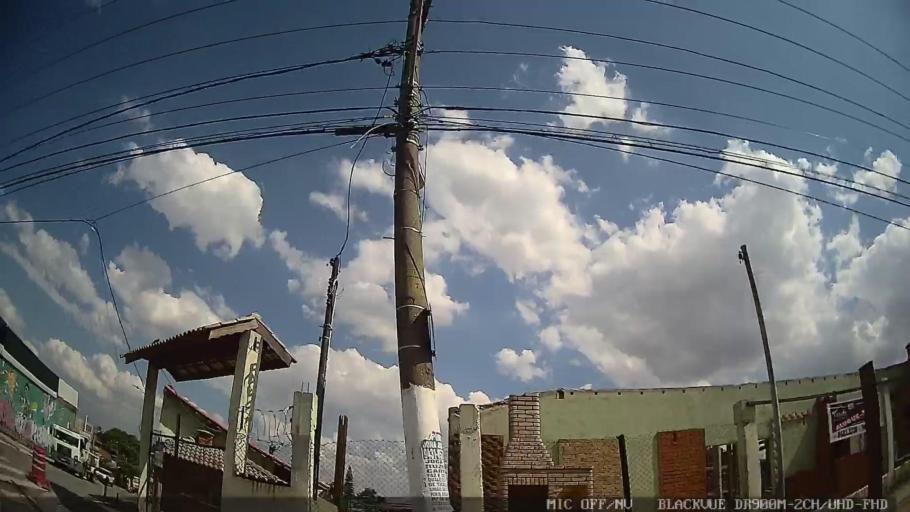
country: BR
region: Sao Paulo
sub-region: Guarulhos
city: Guarulhos
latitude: -23.5128
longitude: -46.5037
